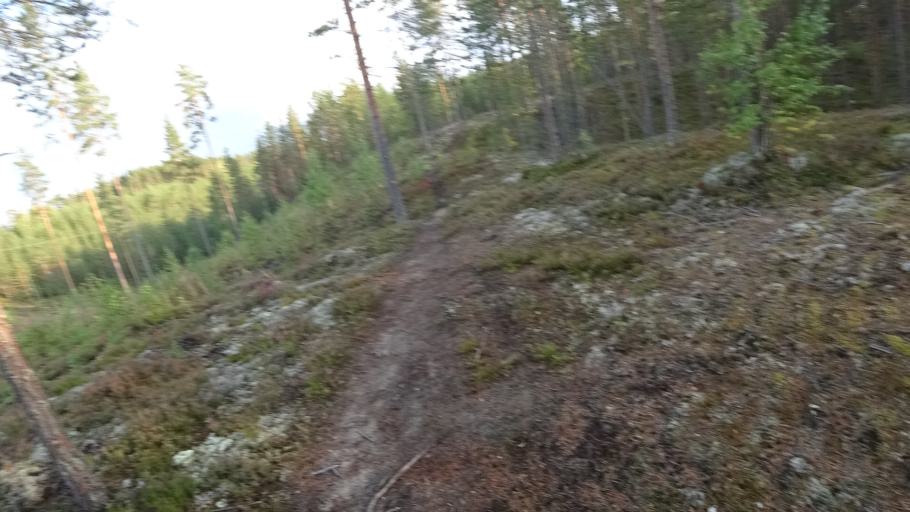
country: FI
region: North Karelia
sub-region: Joensuu
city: Ilomantsi
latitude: 62.6332
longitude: 31.0804
